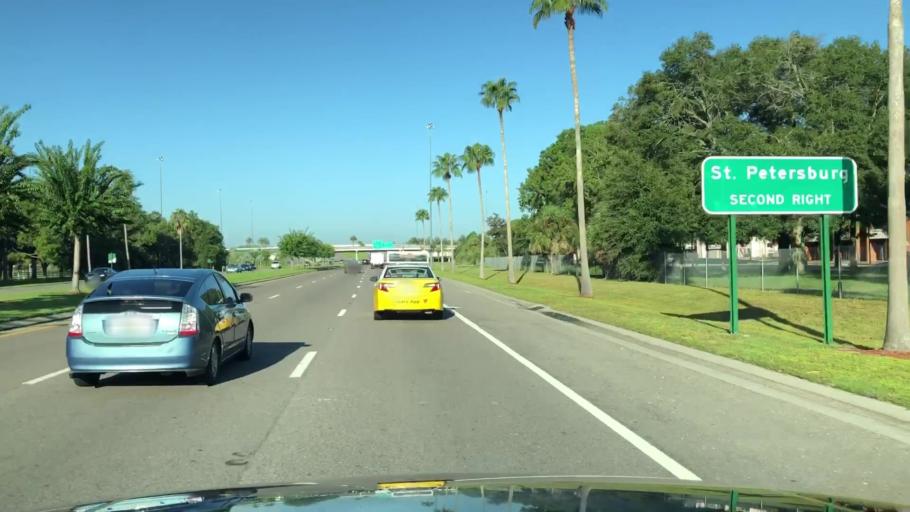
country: US
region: Florida
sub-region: Osceola County
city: Celebration
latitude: 28.3329
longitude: -81.5373
